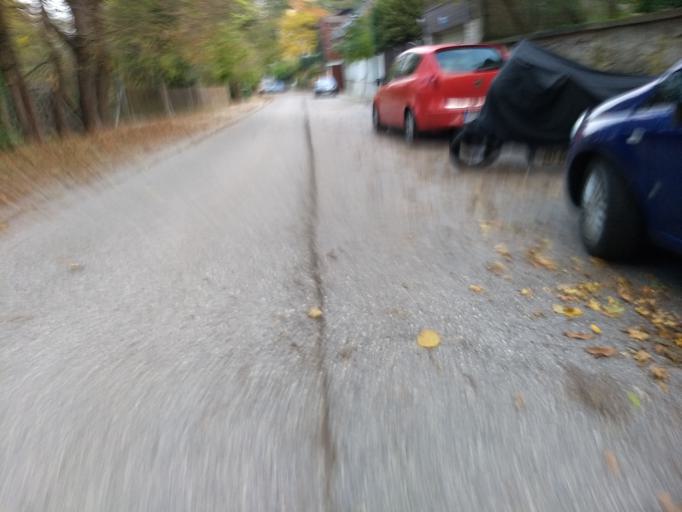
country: AT
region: Lower Austria
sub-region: Politischer Bezirk Modling
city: Perchtoldsdorf
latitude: 48.1298
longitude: 16.2522
